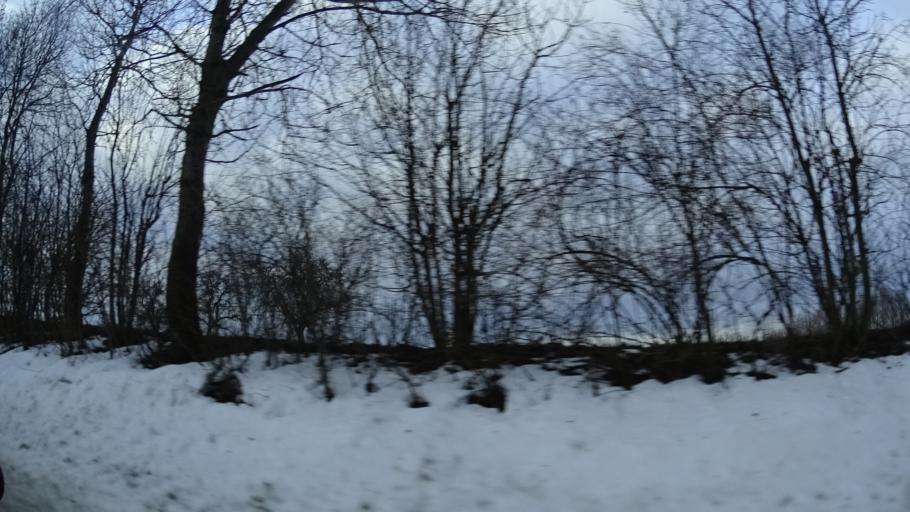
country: DE
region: Baden-Wuerttemberg
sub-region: Karlsruhe Region
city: Fahrenbach
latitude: 49.4597
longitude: 9.0985
